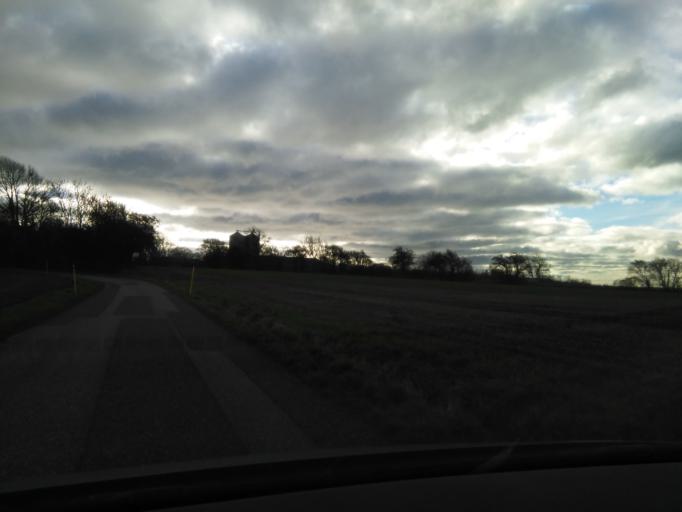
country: DK
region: Central Jutland
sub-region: Odder Kommune
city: Odder
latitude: 55.9083
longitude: 10.1872
